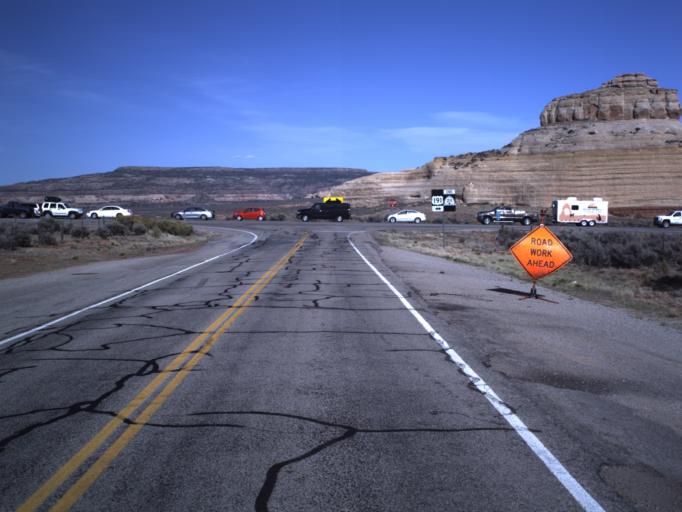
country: US
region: Utah
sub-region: San Juan County
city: Monticello
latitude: 38.0739
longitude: -109.3515
